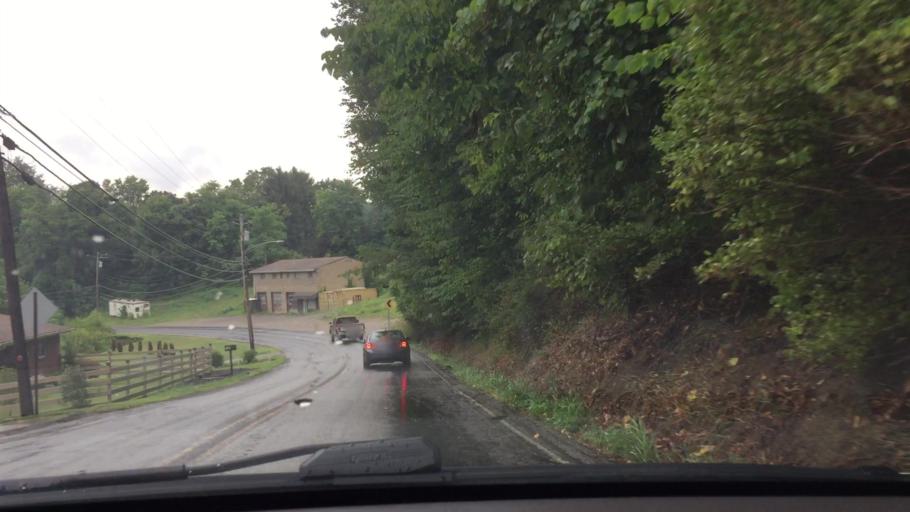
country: US
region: Pennsylvania
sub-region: Washington County
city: Cecil-Bishop
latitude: 40.3164
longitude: -80.1990
